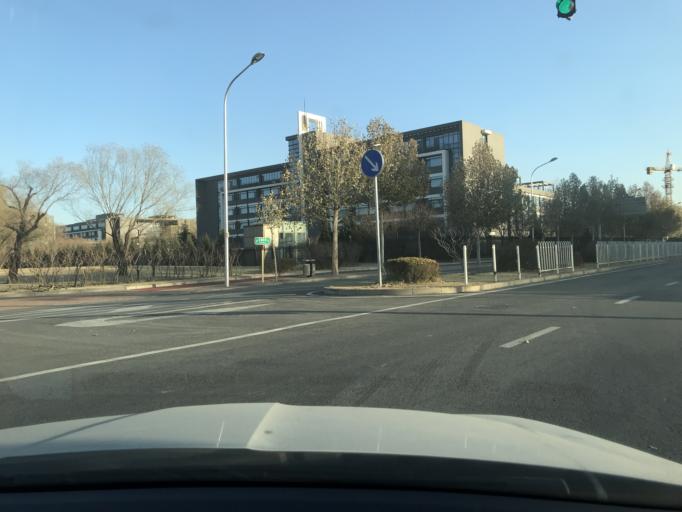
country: CN
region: Beijing
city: Xibeiwang
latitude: 40.0718
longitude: 116.2456
